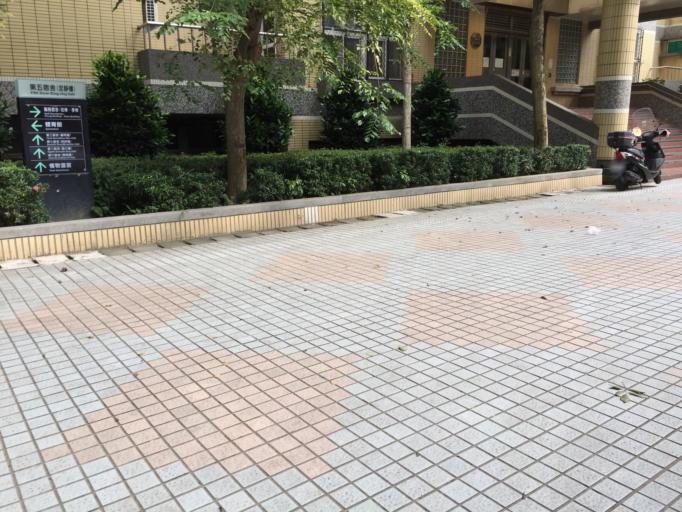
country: TW
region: Taiwan
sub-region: Changhua
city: Chang-hua
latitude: 24.0801
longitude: 120.5592
